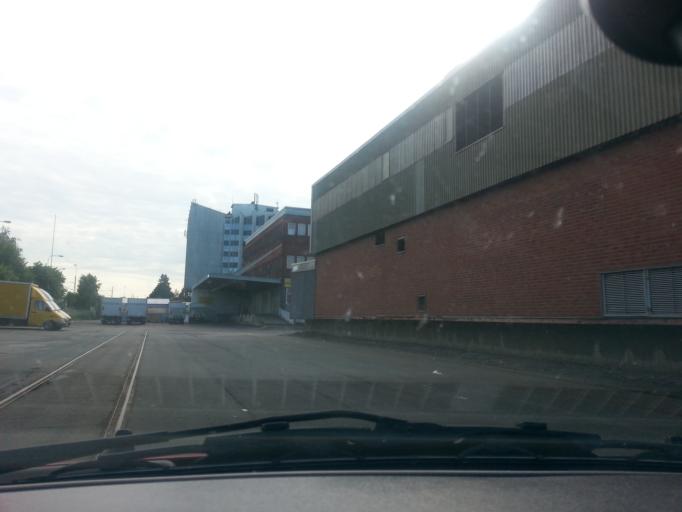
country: SE
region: Vaestra Goetaland
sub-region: Goteborg
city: Goeteborg
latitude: 57.7204
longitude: 11.9991
